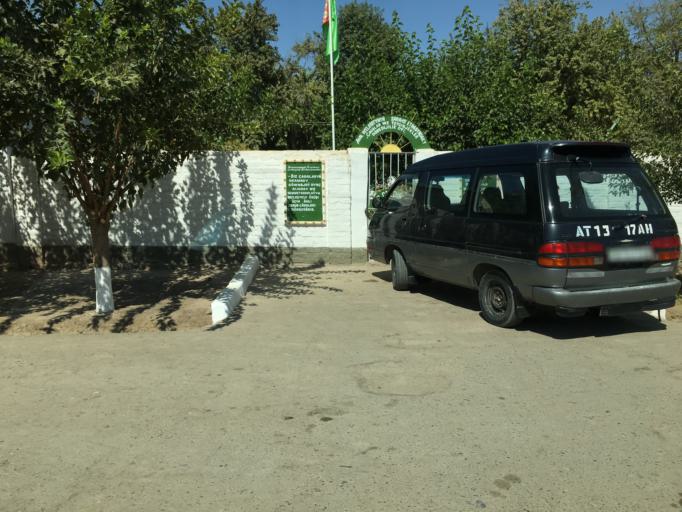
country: IR
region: Razavi Khorasan
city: Sarakhs
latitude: 36.5291
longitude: 61.2112
